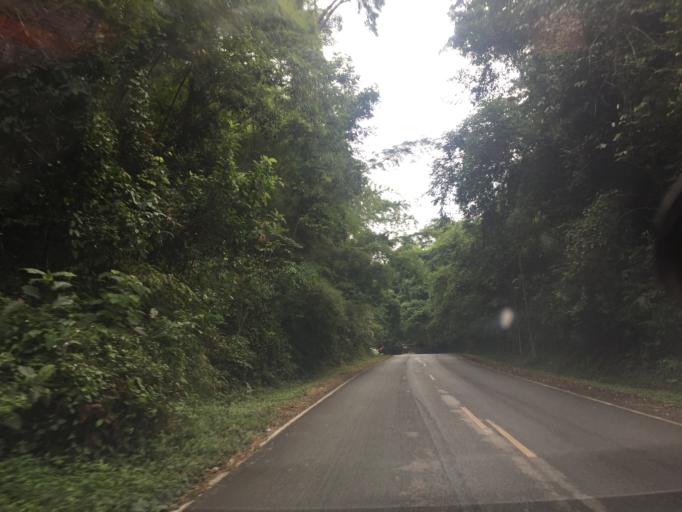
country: TH
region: Lampang
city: Mueang Pan
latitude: 18.8350
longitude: 99.4760
